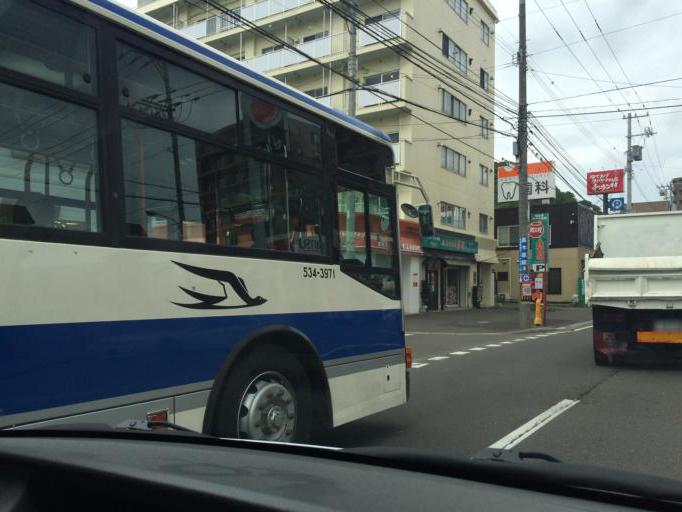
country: JP
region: Hokkaido
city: Sapporo
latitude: 43.0424
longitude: 141.3260
